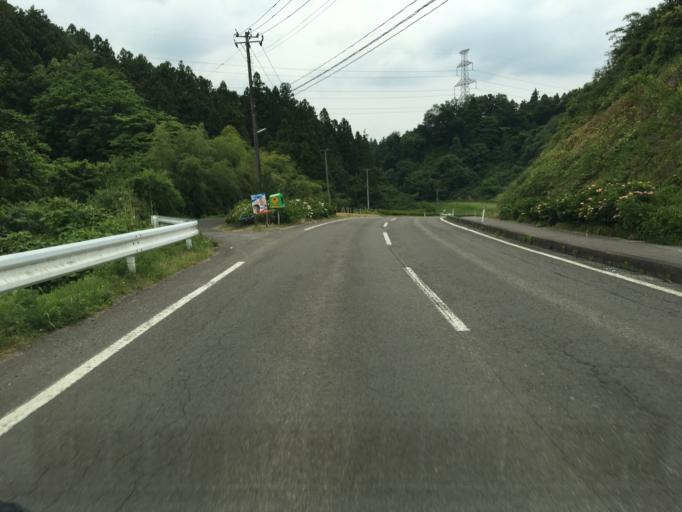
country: JP
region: Fukushima
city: Nihommatsu
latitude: 37.6191
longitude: 140.5444
